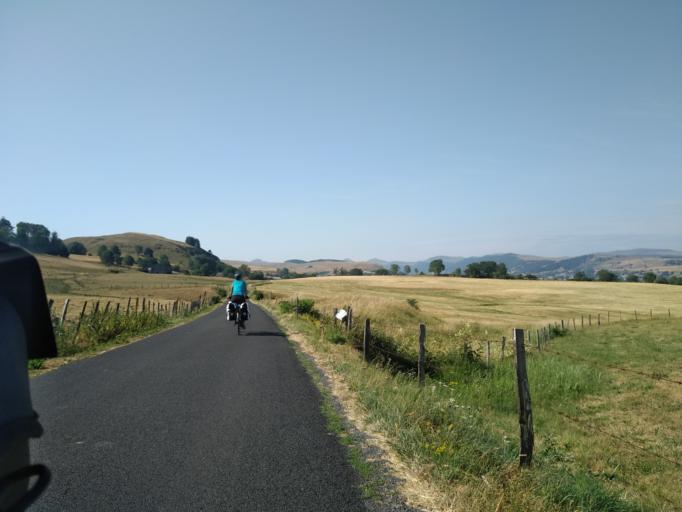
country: FR
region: Auvergne
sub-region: Departement du Cantal
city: Riom-es-Montagnes
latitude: 45.2520
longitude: 2.7435
